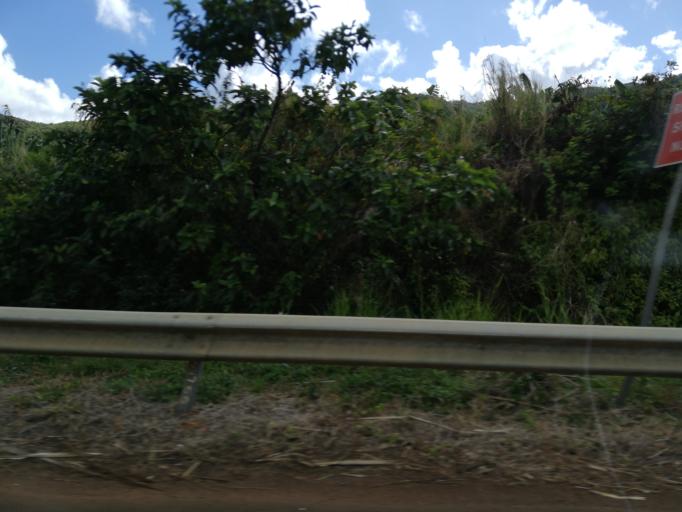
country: MU
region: Grand Port
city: Mahebourg
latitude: -20.3918
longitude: 57.6908
